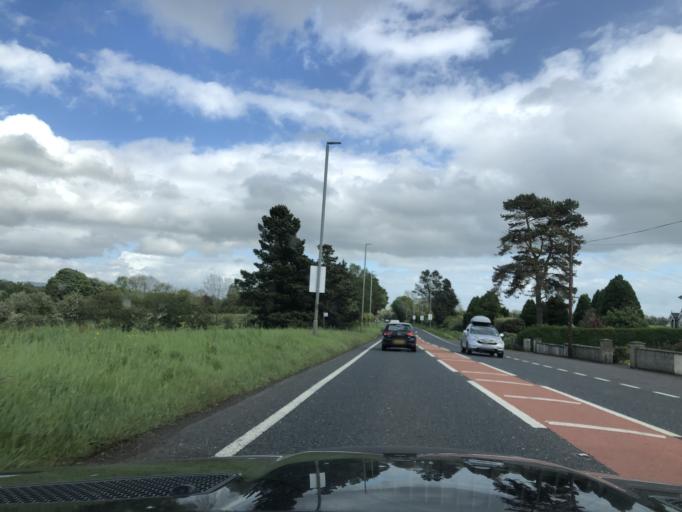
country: GB
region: Northern Ireland
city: Dunloy
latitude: 55.0491
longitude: -6.4338
